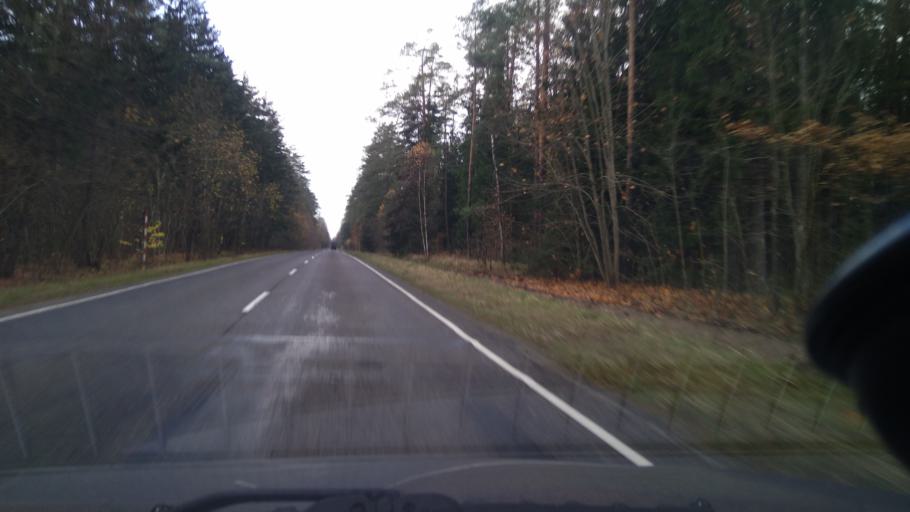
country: BY
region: Minsk
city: Urechcha
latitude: 53.2062
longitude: 27.7890
